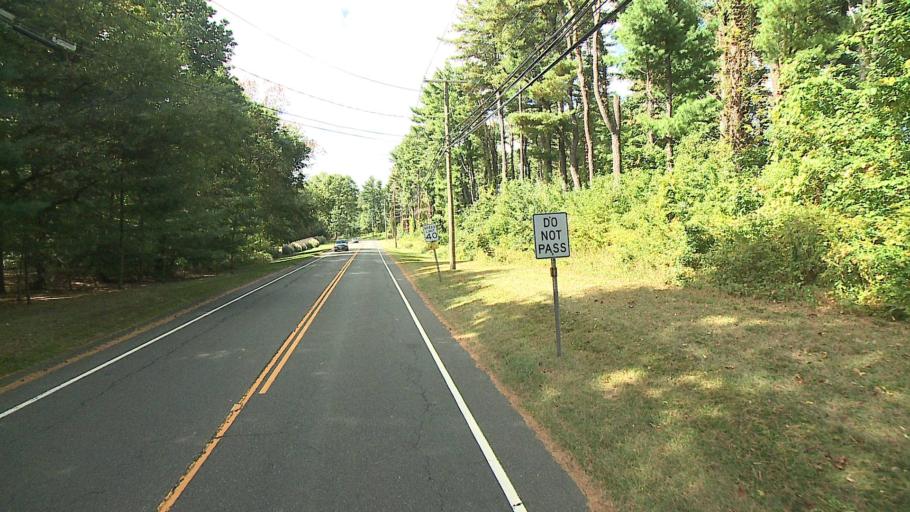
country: US
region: Connecticut
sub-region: Fairfield County
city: Wilton
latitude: 41.1746
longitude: -73.4429
